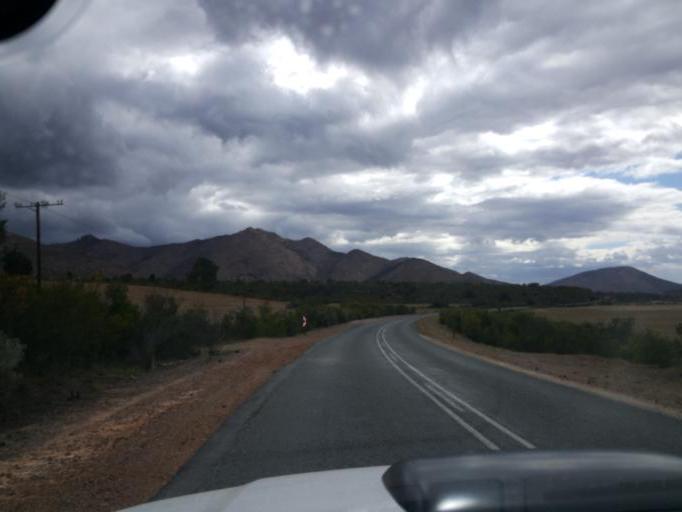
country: ZA
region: Western Cape
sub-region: Eden District Municipality
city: George
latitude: -33.8277
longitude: 22.4026
